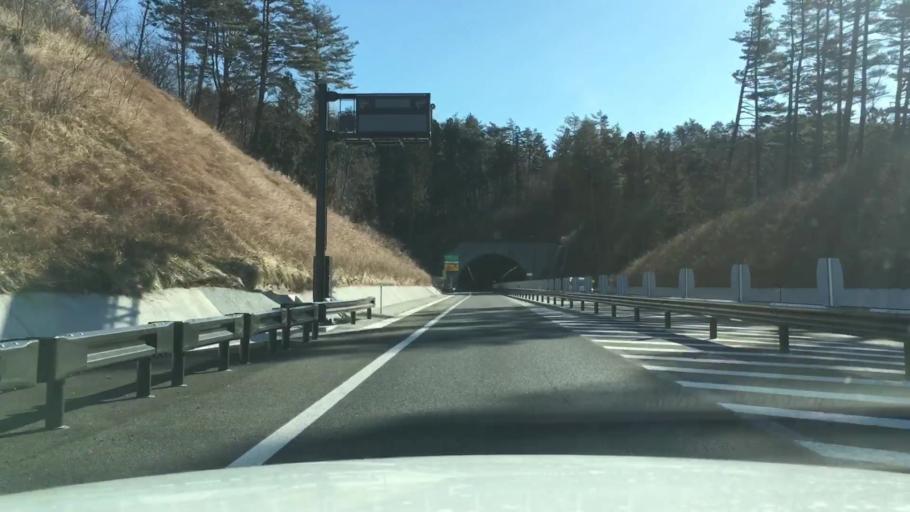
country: JP
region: Iwate
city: Yamada
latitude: 39.5154
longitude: 141.9425
